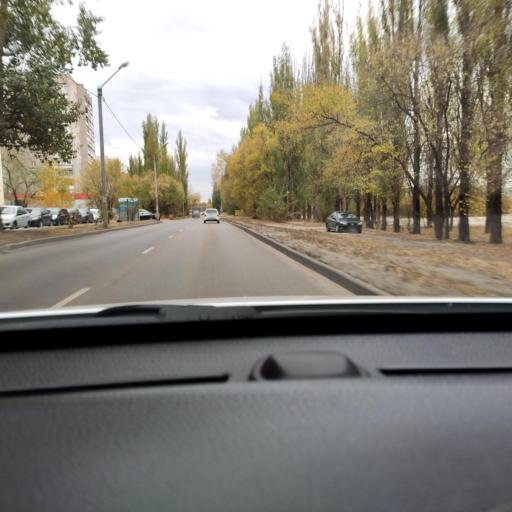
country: RU
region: Voronezj
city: Voronezh
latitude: 51.6950
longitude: 39.2558
